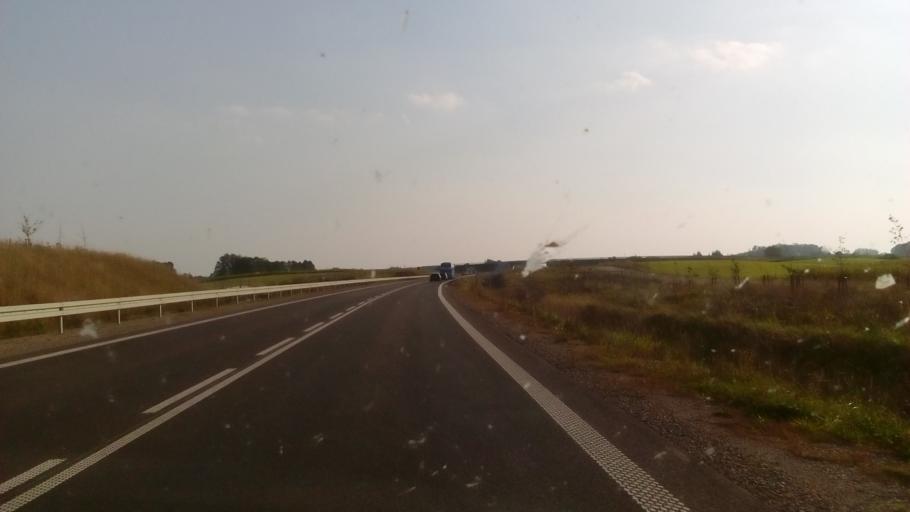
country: PL
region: Podlasie
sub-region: Powiat grajewski
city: Rajgrod
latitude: 53.7699
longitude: 22.8332
